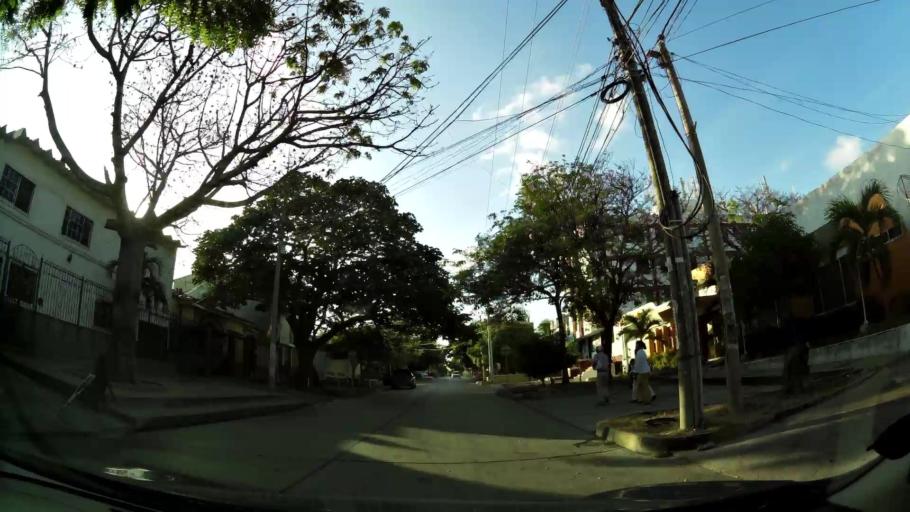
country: CO
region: Atlantico
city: Barranquilla
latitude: 10.9830
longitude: -74.7941
